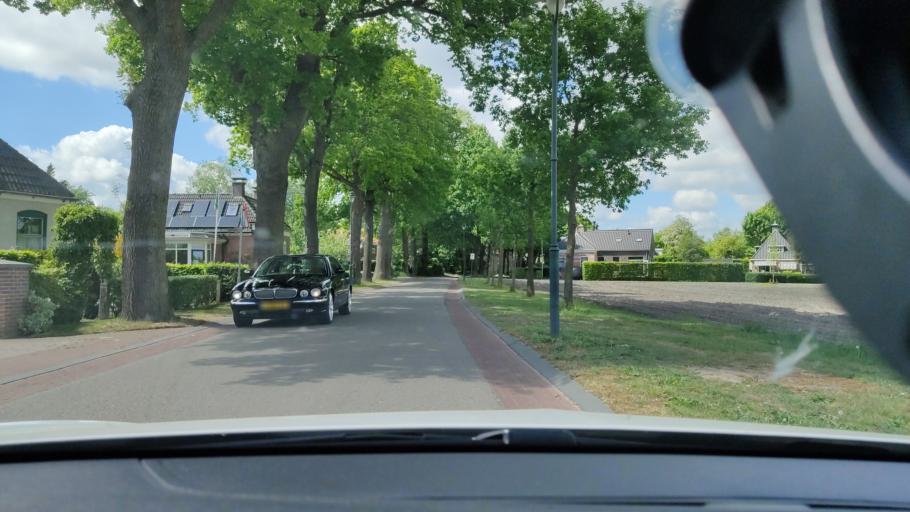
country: NL
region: Drenthe
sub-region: Gemeente Tynaarlo
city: Zuidlaren
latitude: 53.1173
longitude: 6.6686
